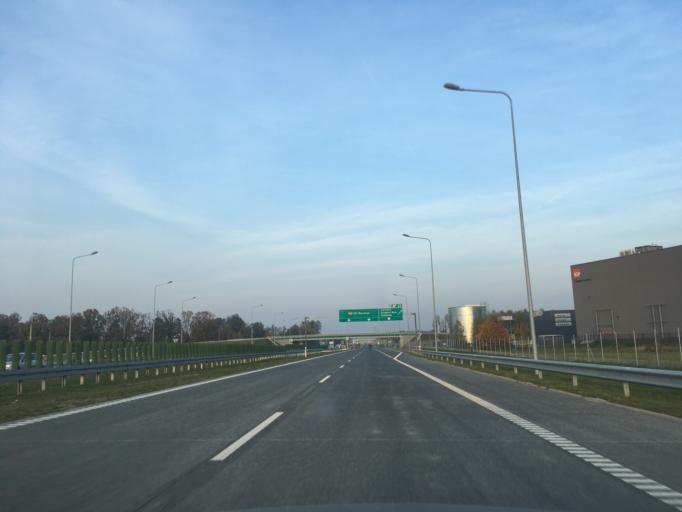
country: PL
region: Lodz Voivodeship
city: Zabia Wola
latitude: 52.0498
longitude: 20.7152
